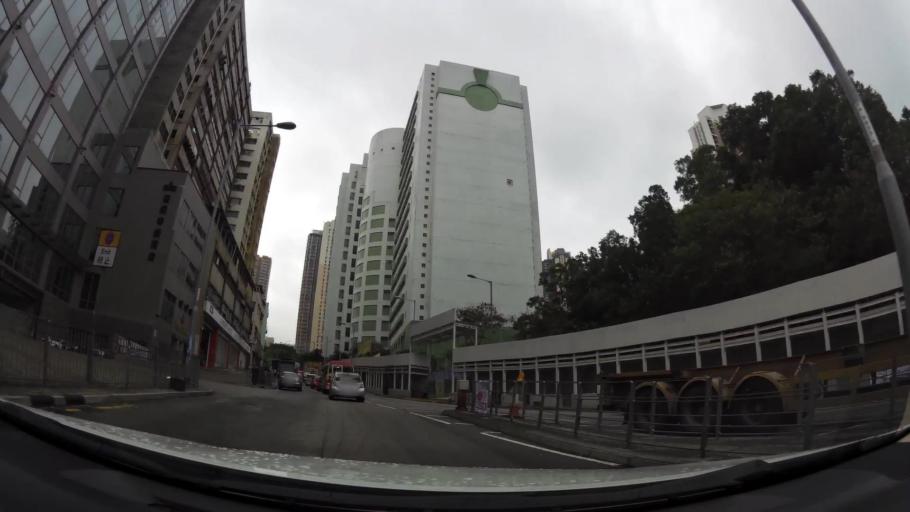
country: HK
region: Tsuen Wan
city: Tsuen Wan
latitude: 22.3707
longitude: 114.1293
